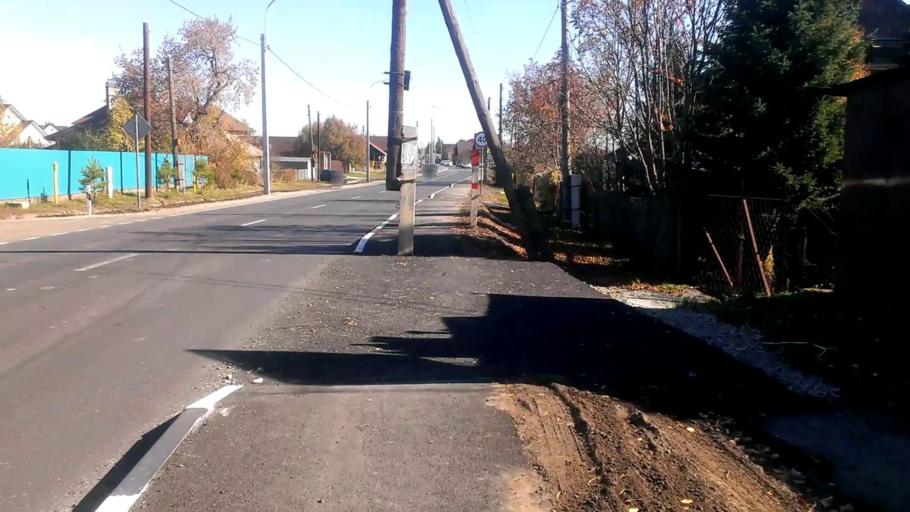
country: RU
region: Altai Krai
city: Sannikovo
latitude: 53.3177
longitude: 83.9481
